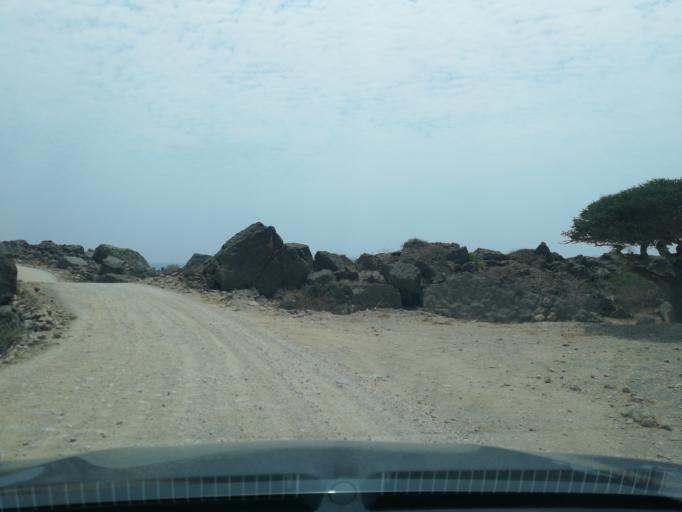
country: OM
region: Zufar
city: Salalah
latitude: 16.8168
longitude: 53.6925
